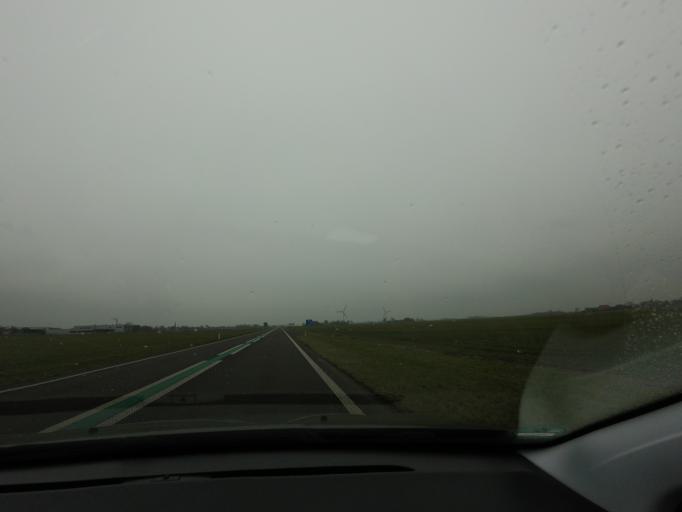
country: NL
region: Friesland
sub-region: Gemeente Littenseradiel
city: Wommels
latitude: 53.1209
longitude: 5.5903
